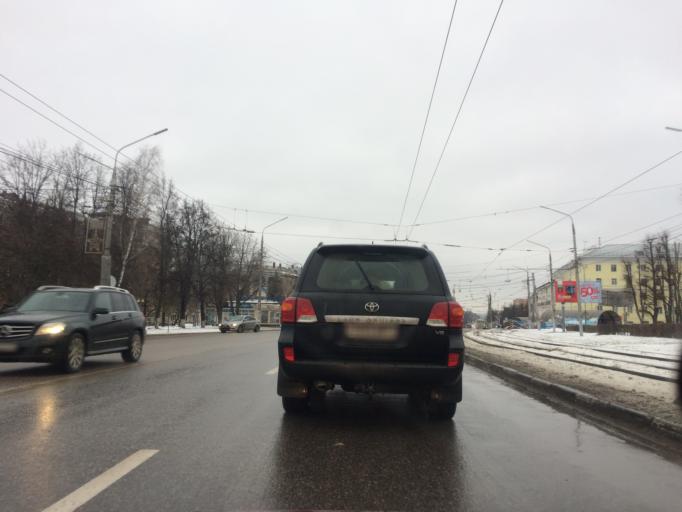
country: RU
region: Tula
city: Mendeleyevskiy
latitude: 54.1656
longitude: 37.5876
